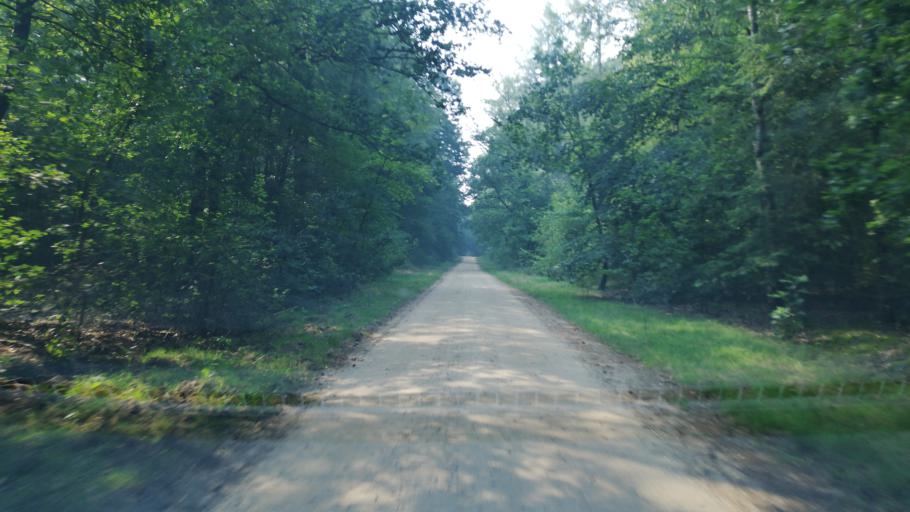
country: NL
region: Gelderland
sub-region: Gemeente Ermelo
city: Ermelo
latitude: 52.2897
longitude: 5.6368
